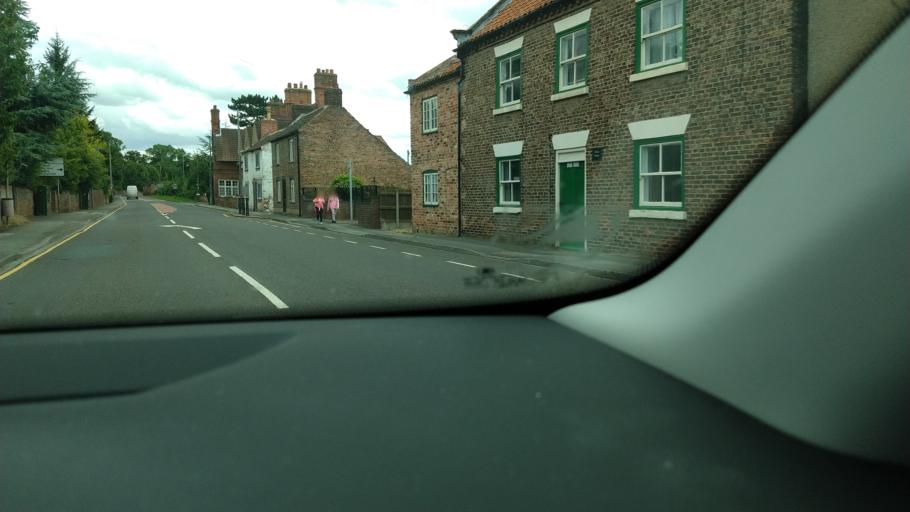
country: GB
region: England
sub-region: East Riding of Yorkshire
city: Snaith
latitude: 53.7074
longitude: -1.0207
